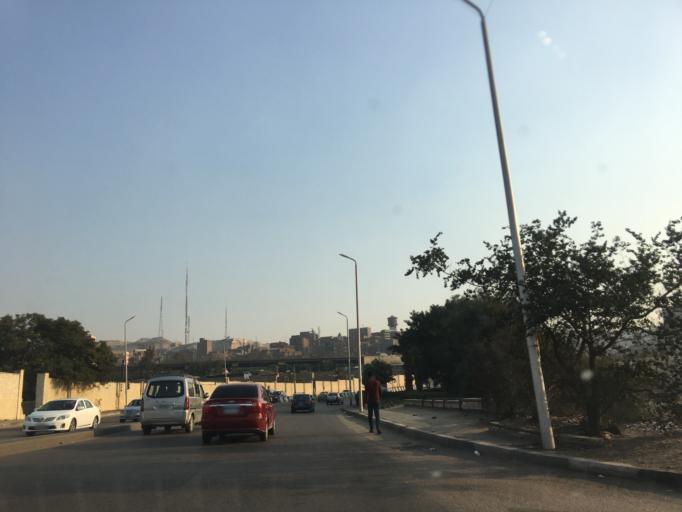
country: EG
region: Muhafazat al Qahirah
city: Cairo
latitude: 30.0366
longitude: 31.2658
